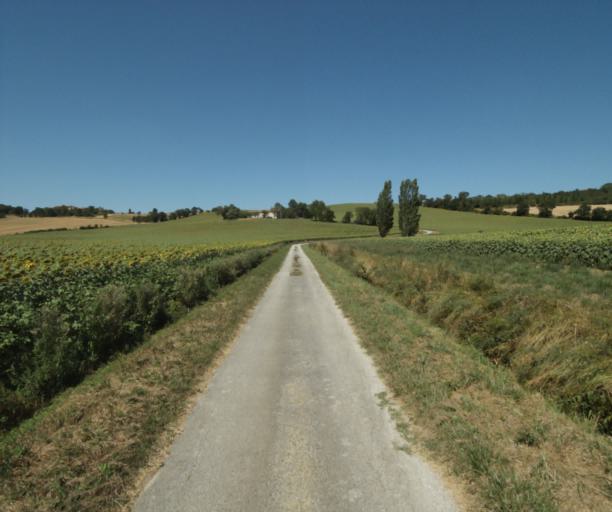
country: FR
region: Midi-Pyrenees
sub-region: Departement de la Haute-Garonne
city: Saint-Felix-Lauragais
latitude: 43.4952
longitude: 1.8798
